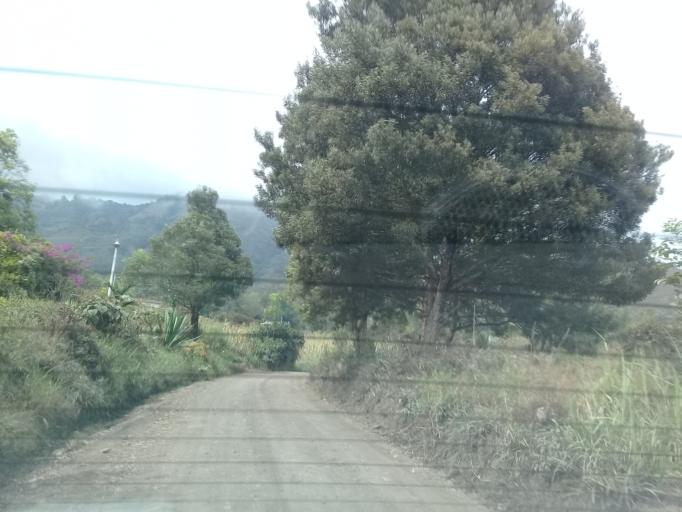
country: CO
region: Cundinamarca
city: Une
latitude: 4.4099
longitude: -73.9877
